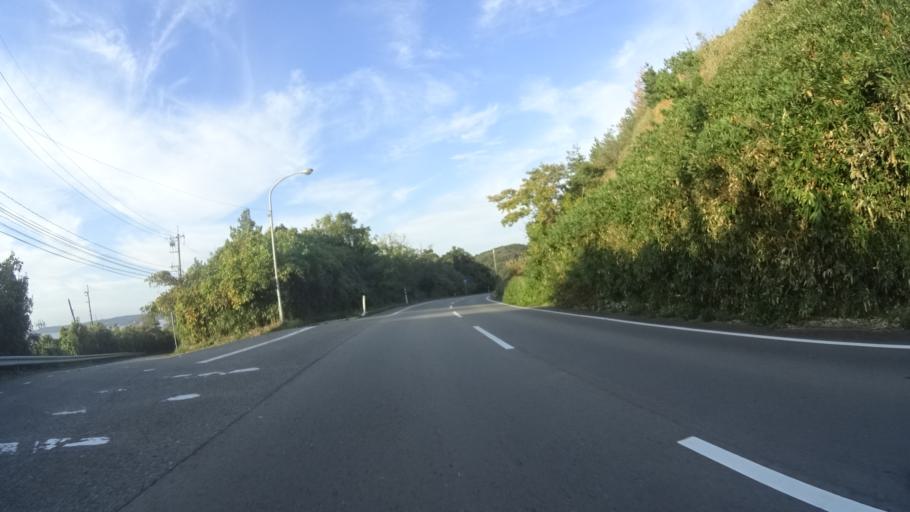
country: JP
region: Ishikawa
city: Hakui
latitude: 37.1131
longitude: 136.7280
